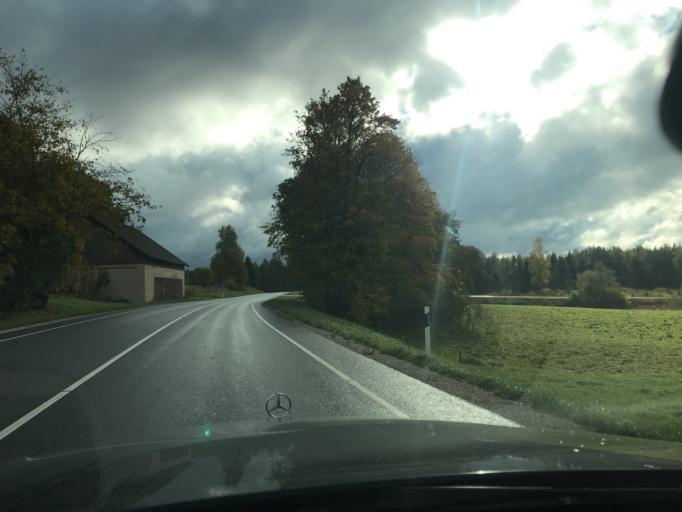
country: EE
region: Valgamaa
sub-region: Torva linn
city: Torva
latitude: 58.0075
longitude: 25.7590
